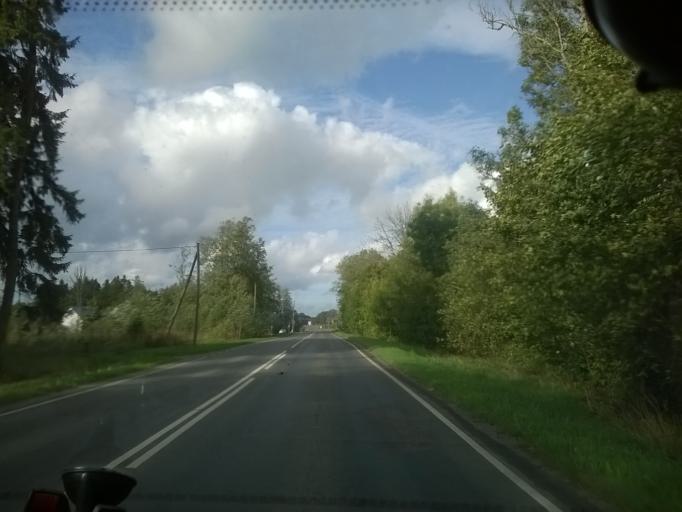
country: EE
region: Harju
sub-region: Rae vald
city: Jueri
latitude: 59.3633
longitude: 24.9240
